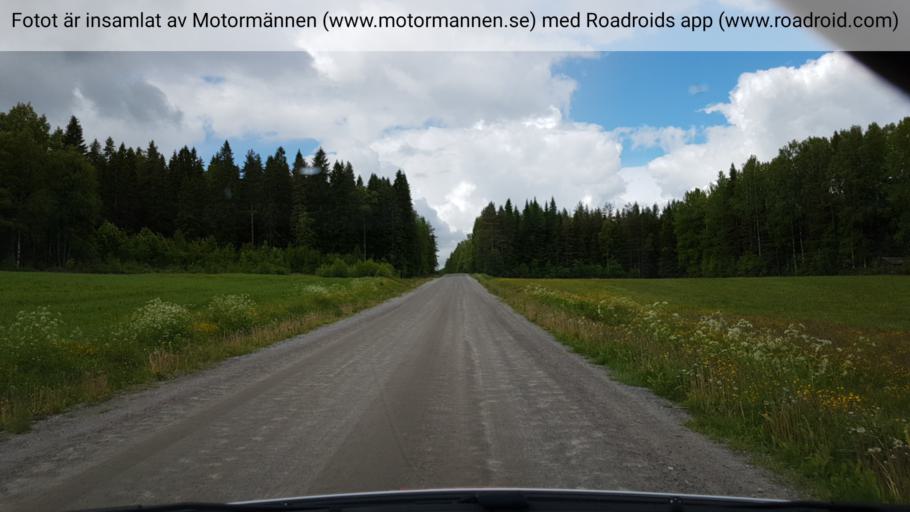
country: SE
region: Vaesterbotten
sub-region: Vannas Kommun
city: Vannasby
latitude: 63.8355
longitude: 19.9830
